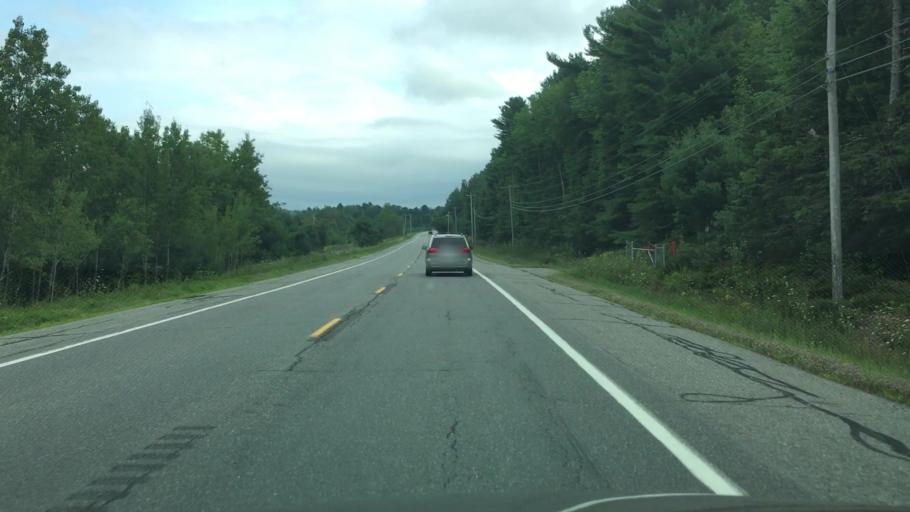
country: US
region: Maine
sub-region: Waldo County
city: Stockton Springs
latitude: 44.5436
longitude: -68.8633
